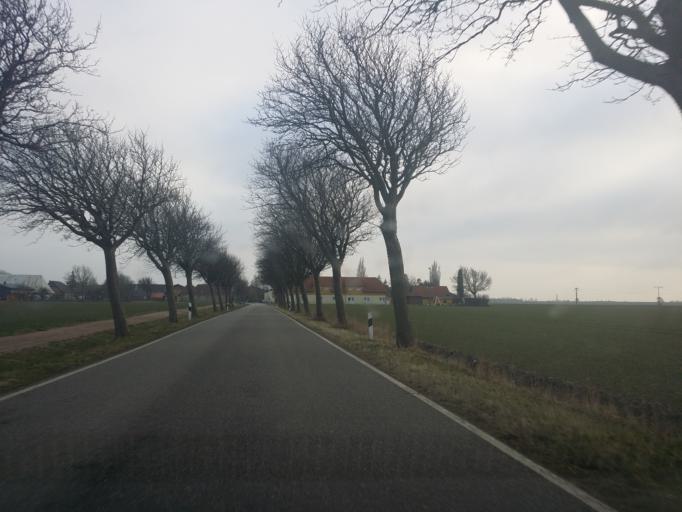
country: DE
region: Schleswig-Holstein
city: Grossenbrode
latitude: 54.4624
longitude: 11.0433
